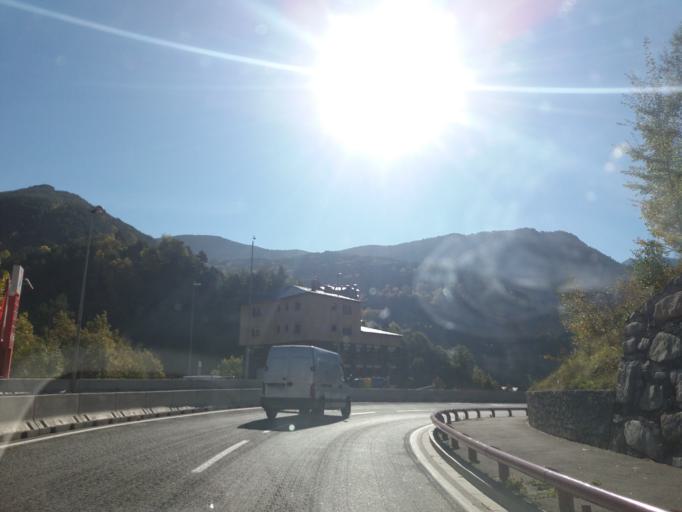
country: AD
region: La Massana
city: la Massana
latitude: 42.5360
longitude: 1.5210
